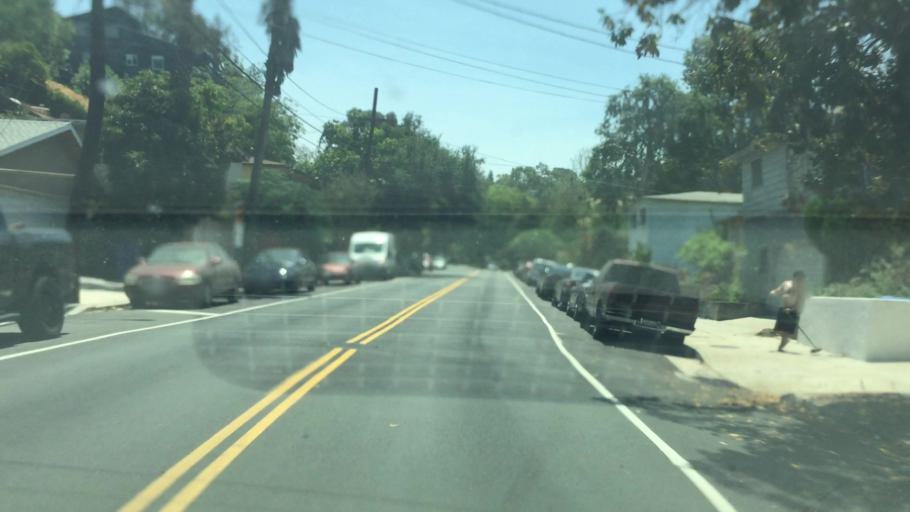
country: US
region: California
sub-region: Los Angeles County
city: Glendale
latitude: 34.1208
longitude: -118.2219
